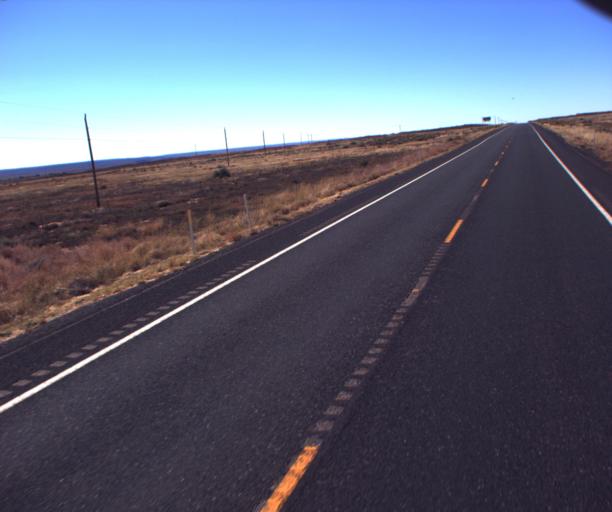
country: US
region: Arizona
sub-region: Coconino County
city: Fredonia
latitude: 36.9229
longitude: -112.5708
